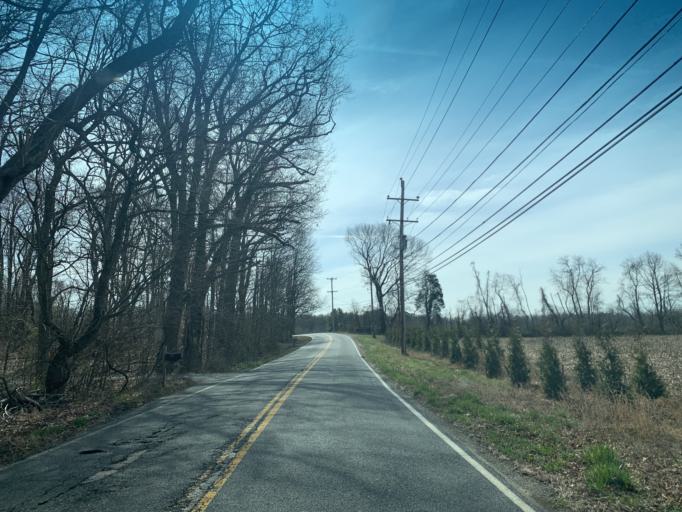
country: US
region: Maryland
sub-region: Cecil County
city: Charlestown
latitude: 39.5617
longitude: -76.0200
